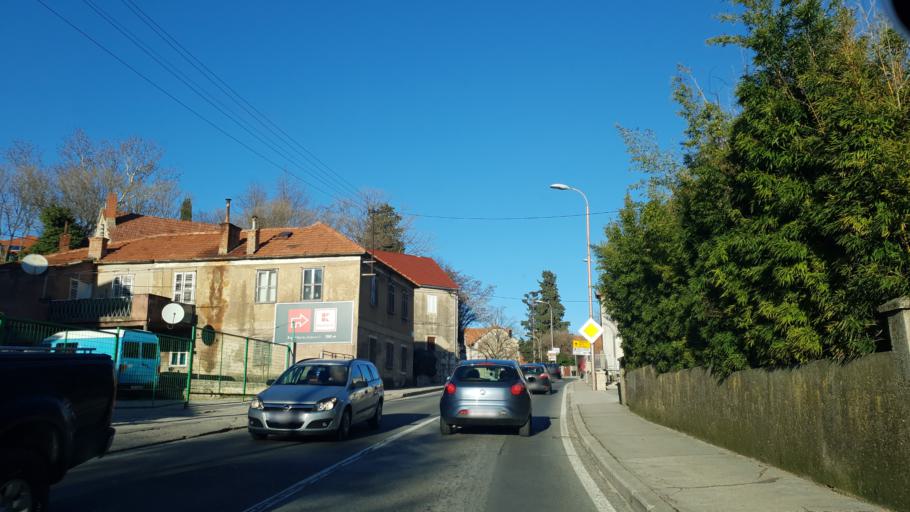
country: HR
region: Splitsko-Dalmatinska
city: Sinj
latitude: 43.7006
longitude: 16.6415
